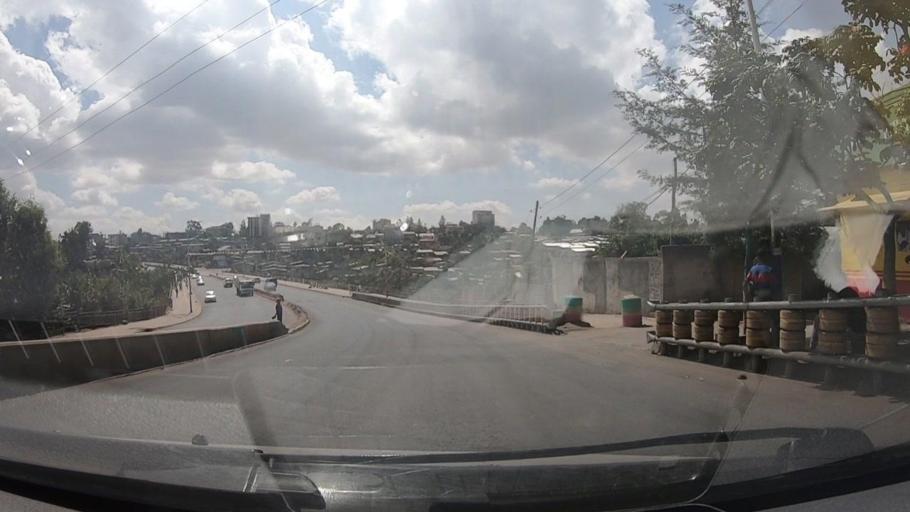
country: ET
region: Adis Abeba
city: Addis Ababa
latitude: 8.9835
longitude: 38.7192
